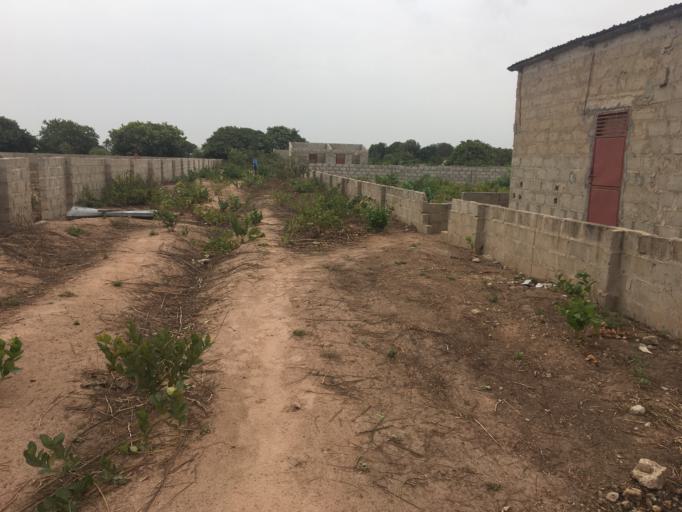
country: GM
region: Western
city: Sukuta
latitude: 13.3140
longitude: -16.7721
